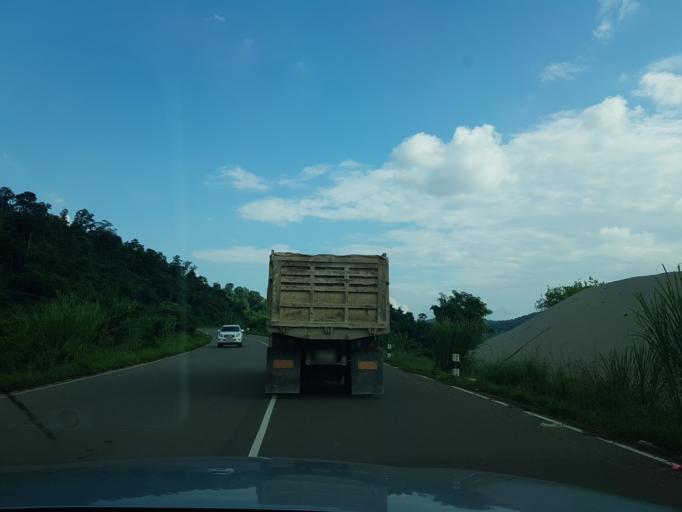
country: TH
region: Nong Khai
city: Pho Tak
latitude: 18.0104
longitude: 102.4018
